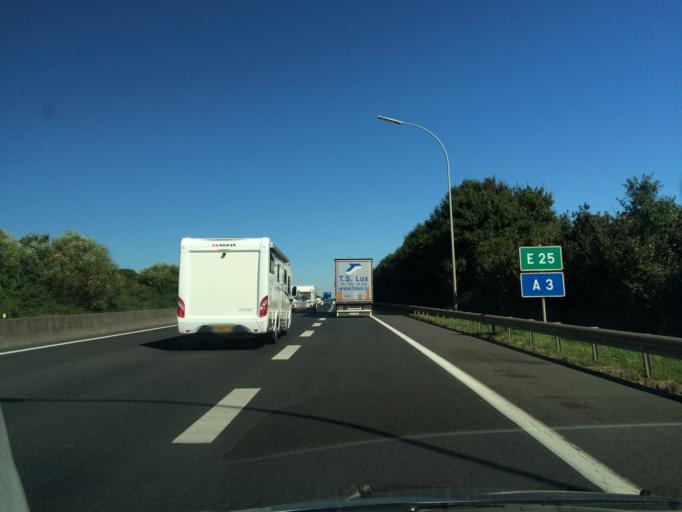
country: LU
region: Luxembourg
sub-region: Canton d'Esch-sur-Alzette
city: Bettembourg
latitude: 49.5008
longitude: 6.1163
